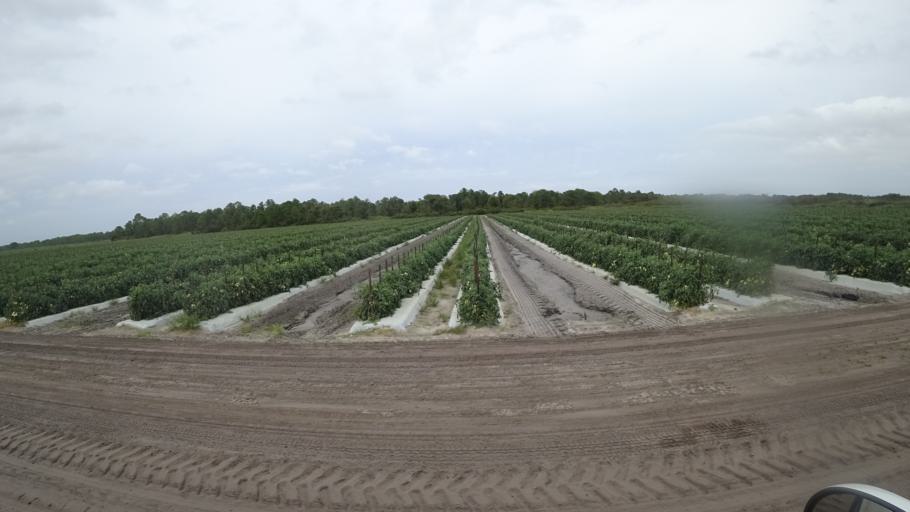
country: US
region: Florida
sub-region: Hillsborough County
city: Wimauma
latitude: 27.5618
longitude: -82.1307
